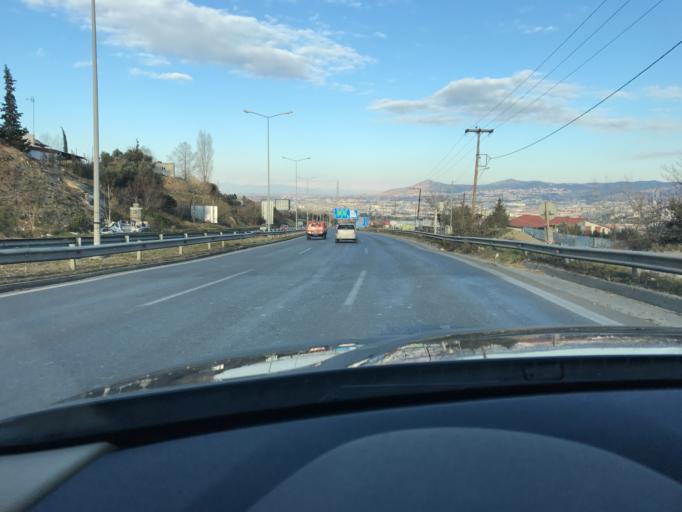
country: GR
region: Central Macedonia
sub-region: Nomos Thessalonikis
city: Polichni
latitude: 40.6633
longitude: 22.9671
